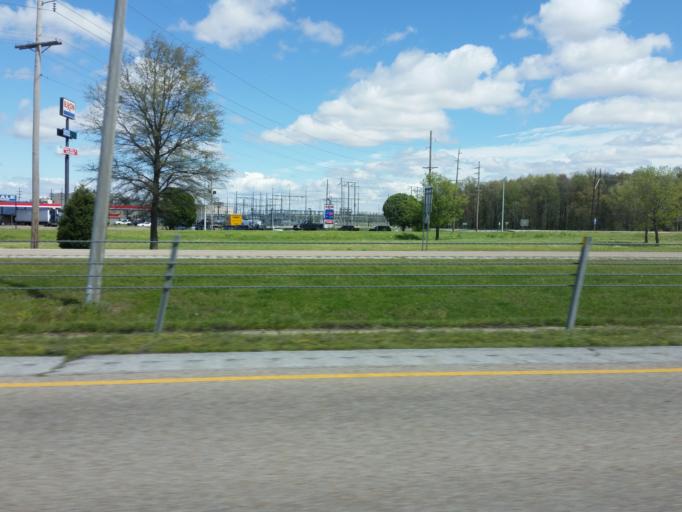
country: US
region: Arkansas
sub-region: Craighead County
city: Jonesboro
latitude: 35.8028
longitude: -90.6266
